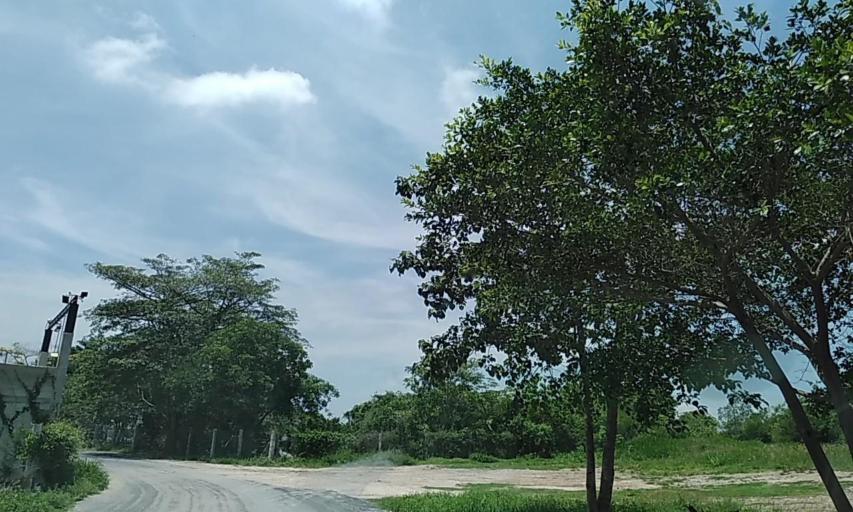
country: MX
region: Veracruz
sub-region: Emiliano Zapata
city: Dos Rios
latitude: 19.4407
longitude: -96.7576
